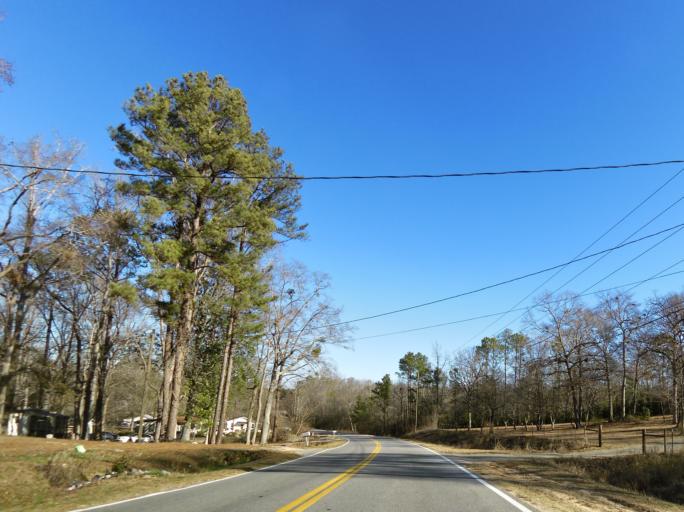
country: US
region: Georgia
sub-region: Bibb County
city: West Point
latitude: 32.7616
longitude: -83.7597
